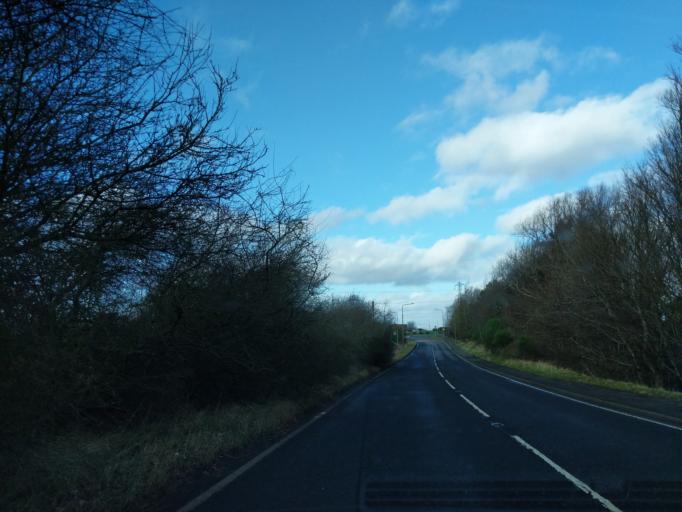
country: GB
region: Scotland
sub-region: West Lothian
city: Kirknewton
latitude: 55.8861
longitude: -3.4228
